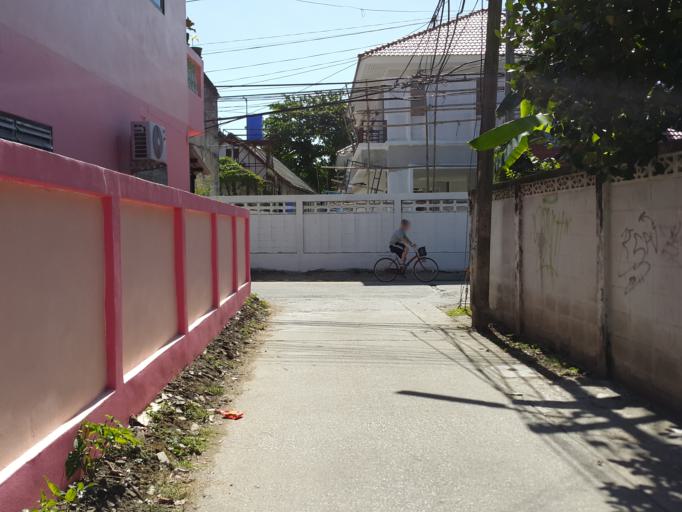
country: TH
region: Chiang Mai
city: Chiang Mai
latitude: 18.7938
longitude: 98.9851
